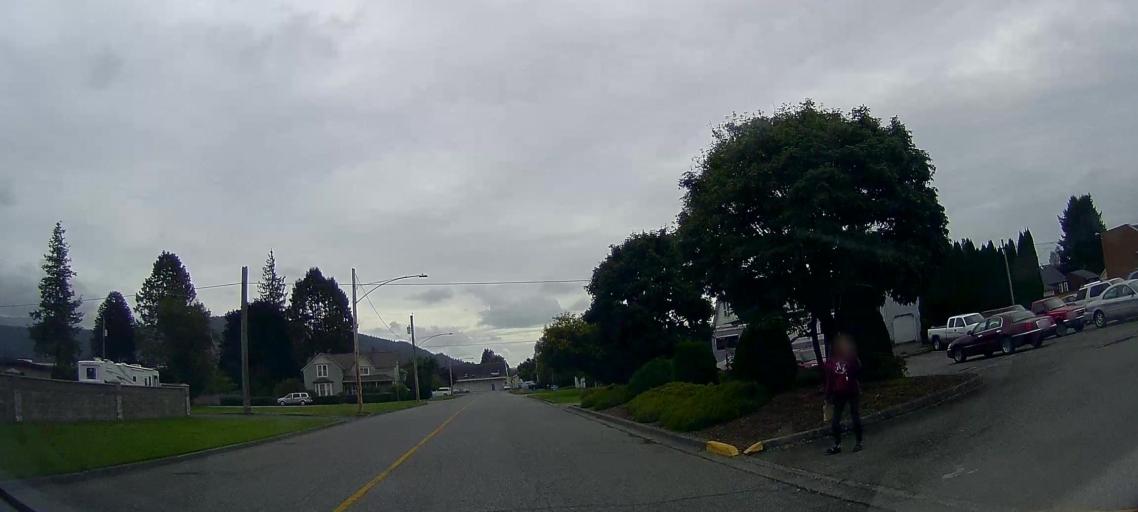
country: US
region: Washington
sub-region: Skagit County
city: Sedro-Woolley
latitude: 48.5023
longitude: -122.2386
